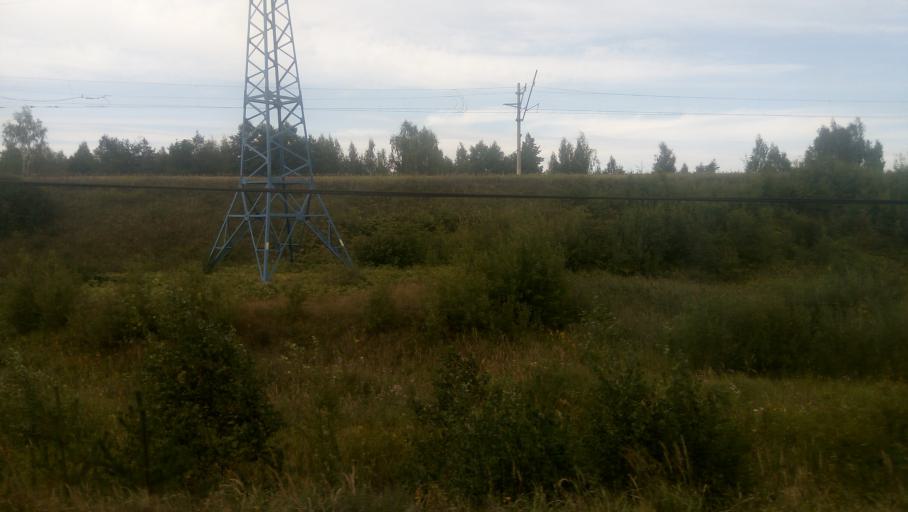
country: RU
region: Moskovskaya
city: Drezna
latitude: 55.7466
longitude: 38.8888
